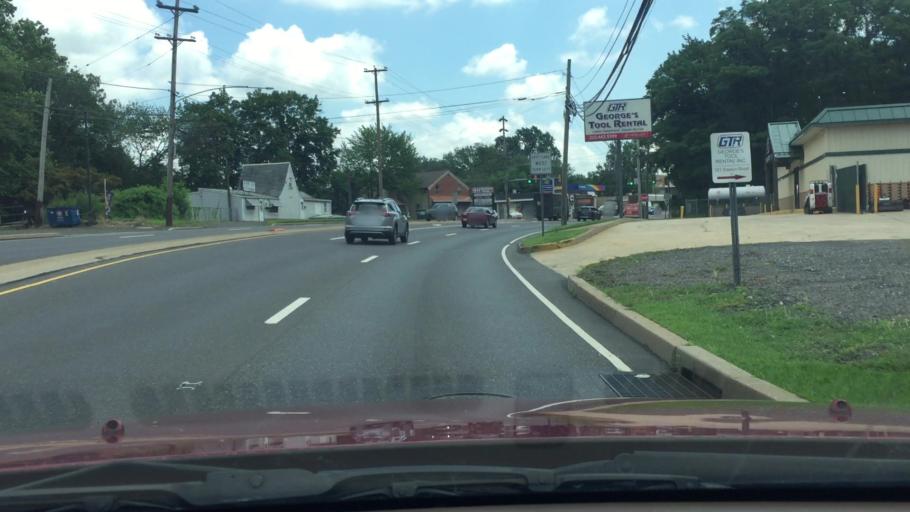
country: US
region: Pennsylvania
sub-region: Montgomery County
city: Horsham
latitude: 40.1786
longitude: -75.1290
